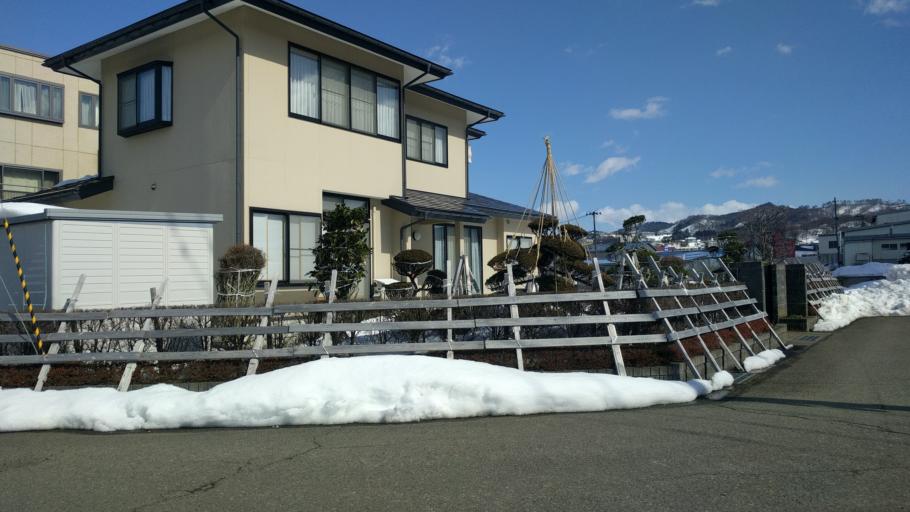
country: JP
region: Fukushima
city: Kitakata
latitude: 37.5190
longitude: 139.9385
